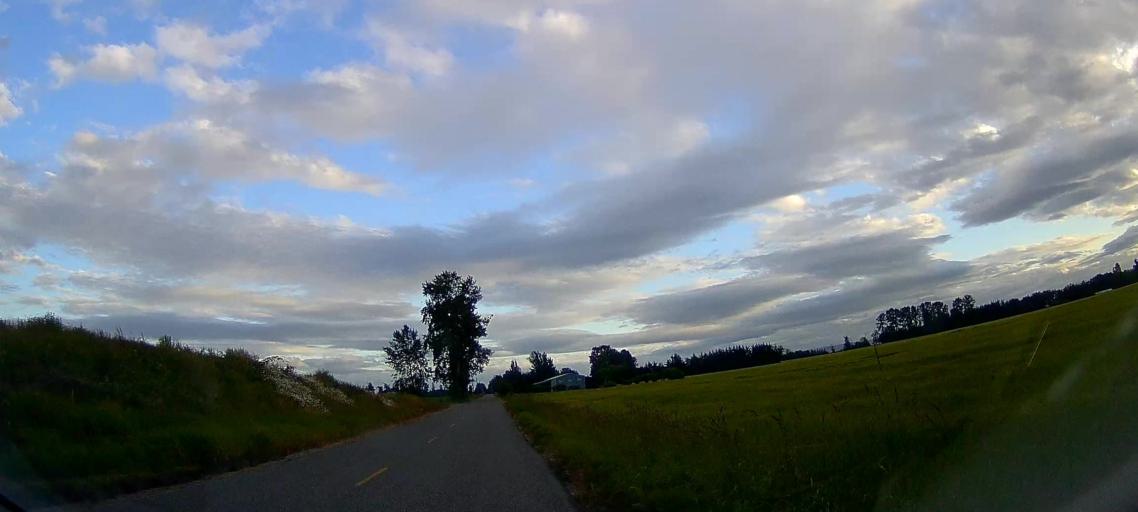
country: US
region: Washington
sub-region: Skagit County
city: Mount Vernon
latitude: 48.3771
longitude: -122.3787
